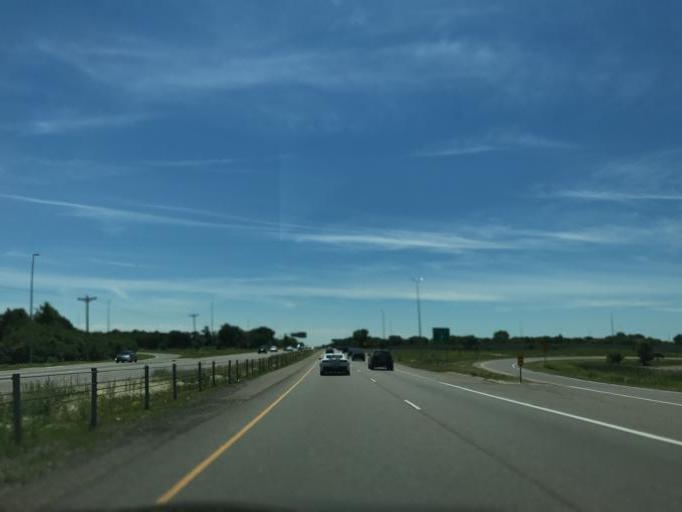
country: US
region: Minnesota
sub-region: Hennepin County
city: Osseo
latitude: 45.0871
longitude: -93.4023
